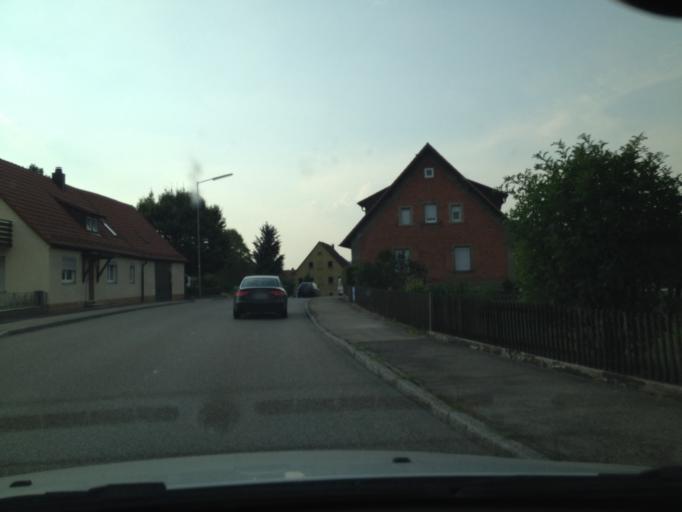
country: DE
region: Bavaria
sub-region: Regierungsbezirk Mittelfranken
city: Dombuhl
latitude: 49.2130
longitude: 10.3054
